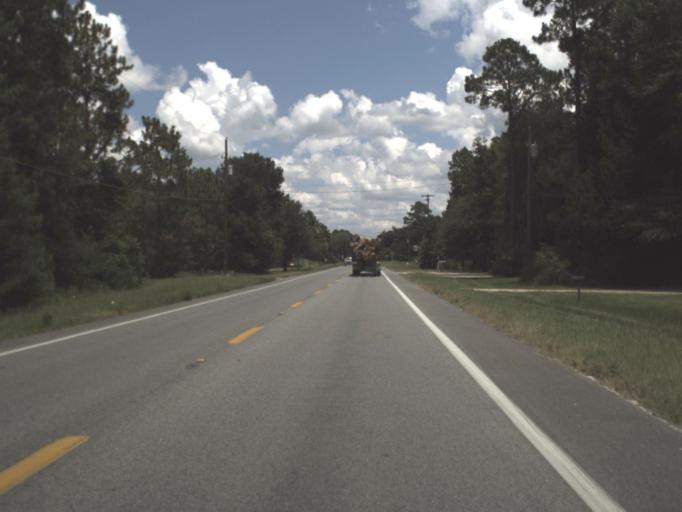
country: US
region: Florida
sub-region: Taylor County
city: Perry
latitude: 30.1030
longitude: -83.6126
